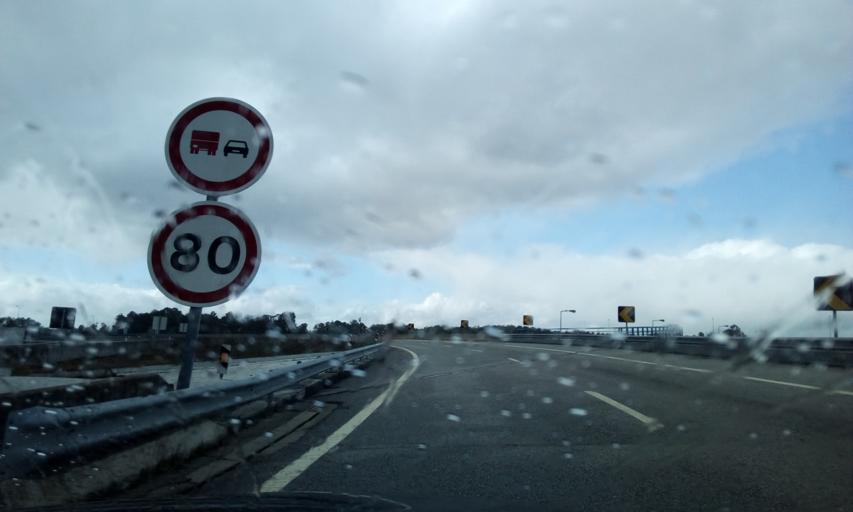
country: PT
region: Viseu
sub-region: Viseu
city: Rio de Loba
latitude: 40.6530
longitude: -7.8618
